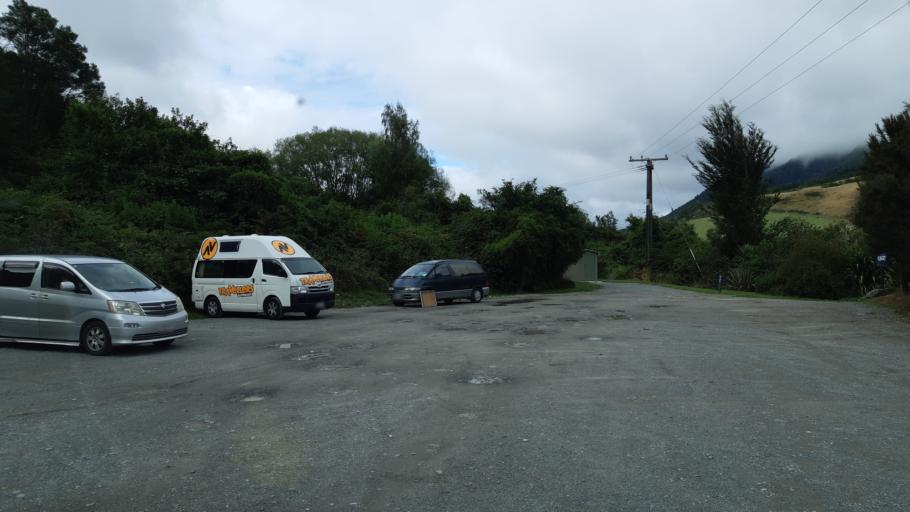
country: NZ
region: West Coast
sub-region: Buller District
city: Westport
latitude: -41.8589
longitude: 172.2533
